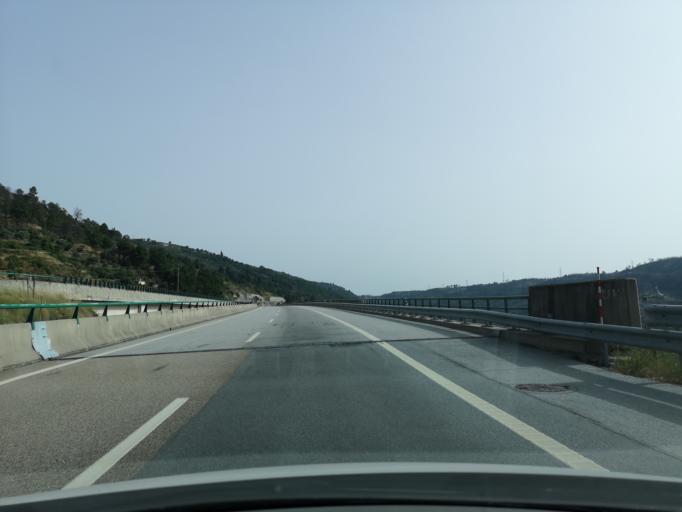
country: PT
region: Guarda
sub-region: Guarda
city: Guarda
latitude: 40.4765
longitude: -7.2569
